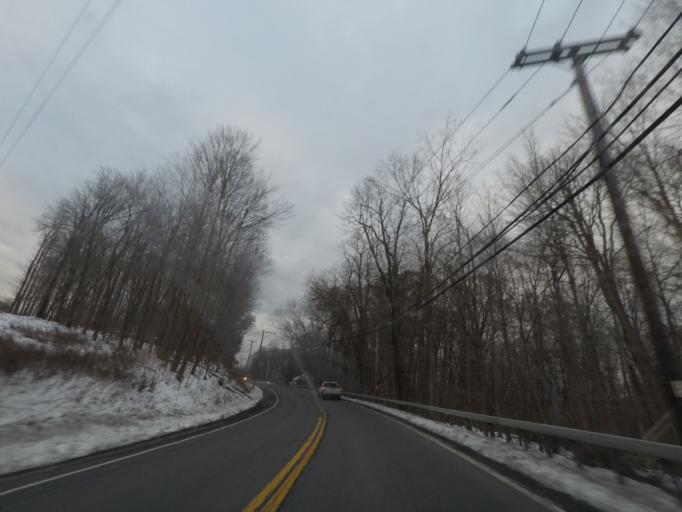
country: US
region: New York
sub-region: Orange County
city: Gardnertown
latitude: 41.5716
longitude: -74.0658
